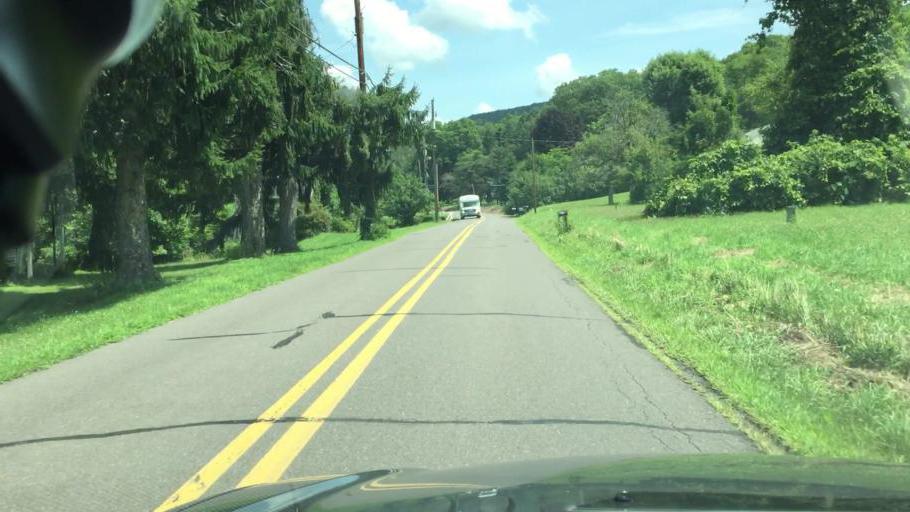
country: US
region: Pennsylvania
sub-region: Luzerne County
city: Harleigh
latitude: 41.0095
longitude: -75.9588
